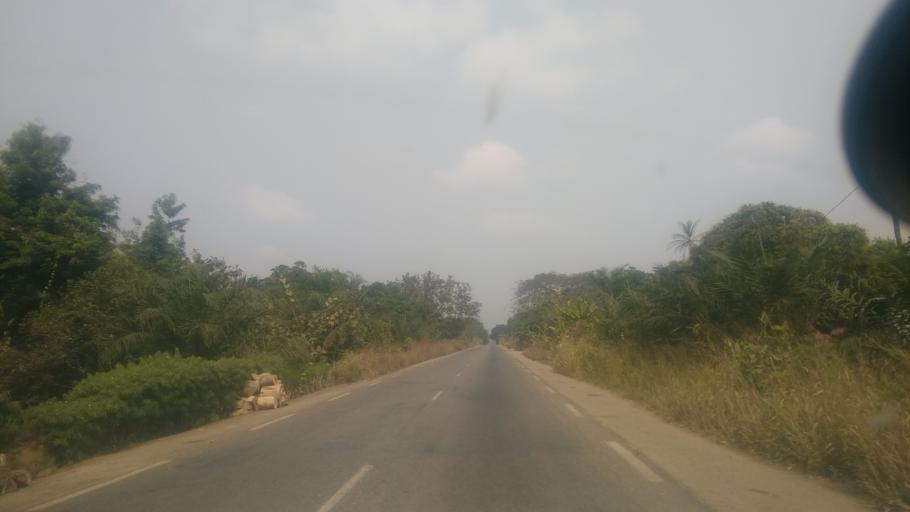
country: CM
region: Centre
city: Bafia
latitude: 4.7100
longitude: 11.2347
